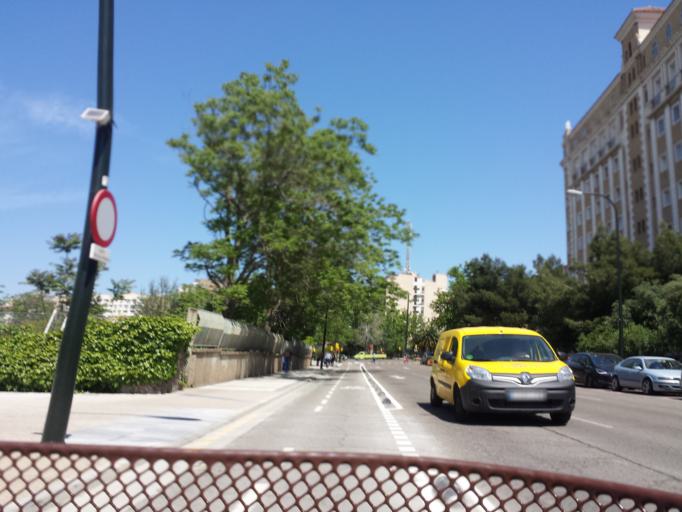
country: ES
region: Aragon
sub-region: Provincia de Zaragoza
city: Almozara
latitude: 41.6526
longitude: -0.8935
